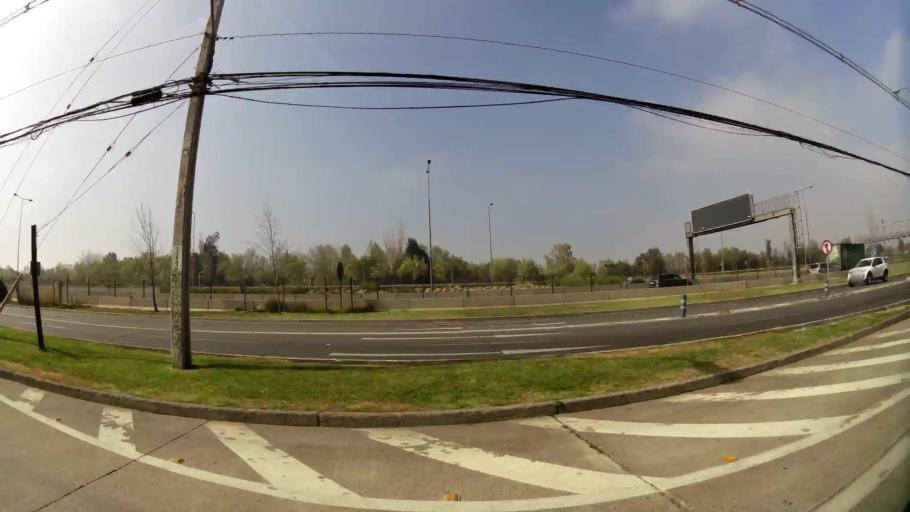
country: CL
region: Santiago Metropolitan
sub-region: Provincia de Santiago
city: Villa Presidente Frei, Nunoa, Santiago, Chile
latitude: -33.3839
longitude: -70.5922
